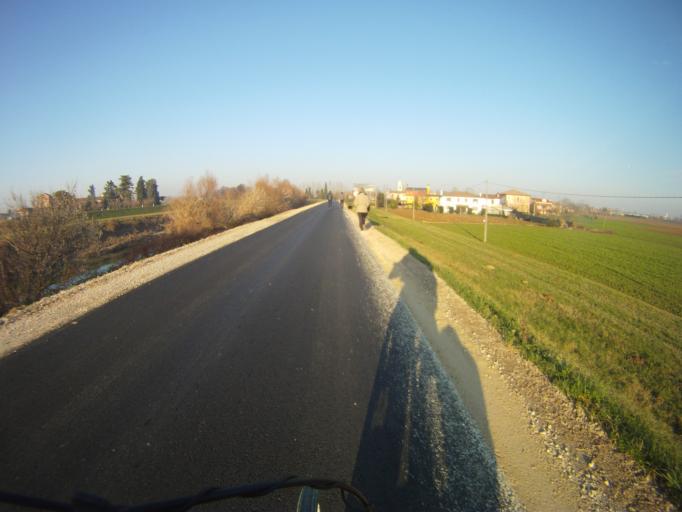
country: IT
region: Veneto
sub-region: Provincia di Padova
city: Legnaro
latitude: 45.3405
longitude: 11.9394
